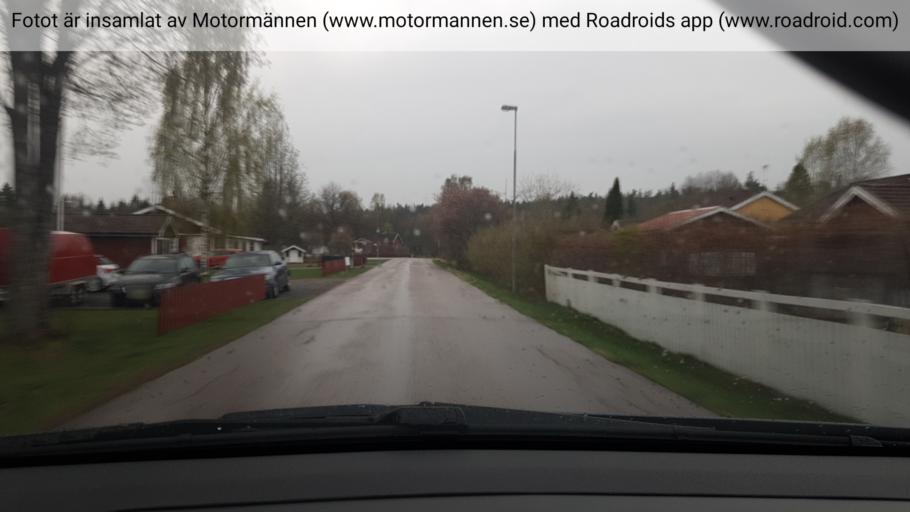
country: SE
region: Dalarna
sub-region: Borlange Kommun
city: Borlaenge
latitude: 60.4822
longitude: 15.3878
